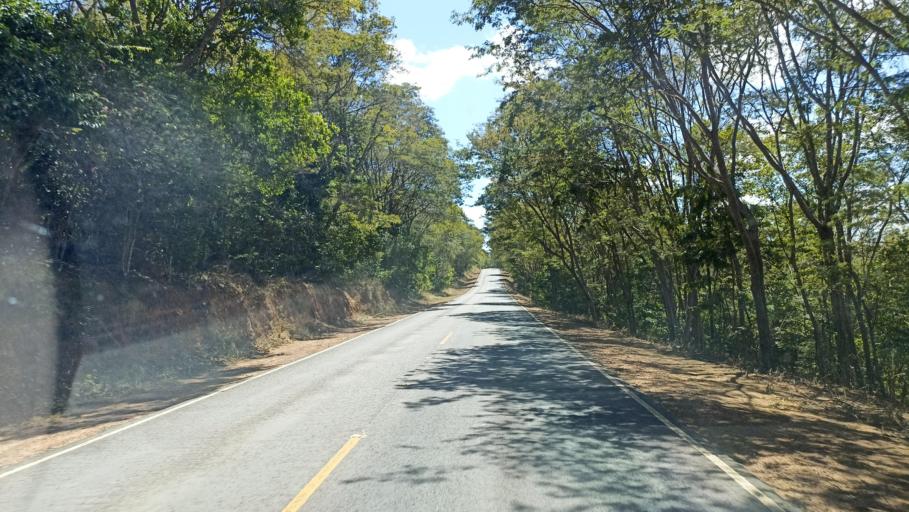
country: BR
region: Bahia
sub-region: Andarai
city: Vera Cruz
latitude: -12.7785
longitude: -41.3296
